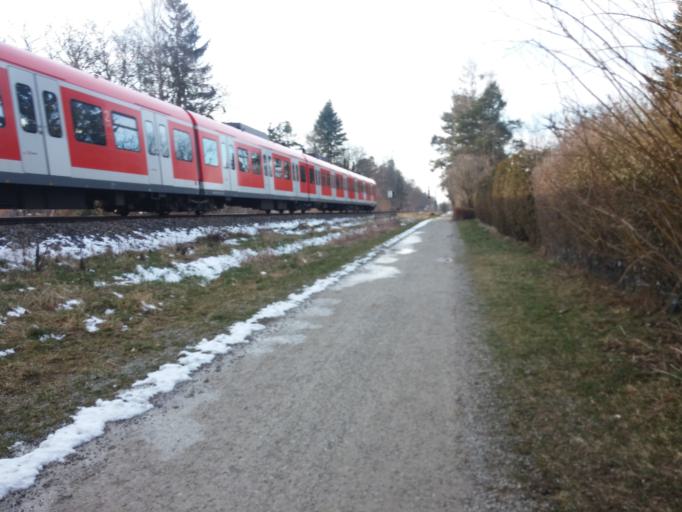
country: DE
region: Bavaria
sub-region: Upper Bavaria
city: Ottobrunn
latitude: 48.0699
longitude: 11.6691
